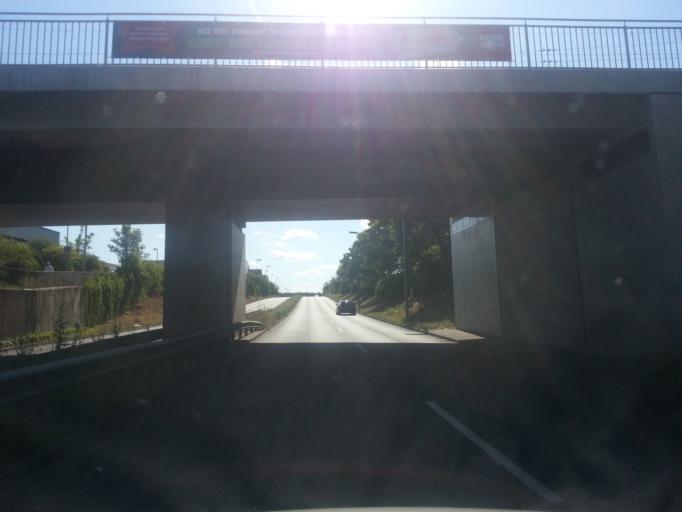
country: DE
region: Hesse
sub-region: Regierungsbezirk Darmstadt
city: Dietzenbach
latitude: 50.0162
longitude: 8.7882
